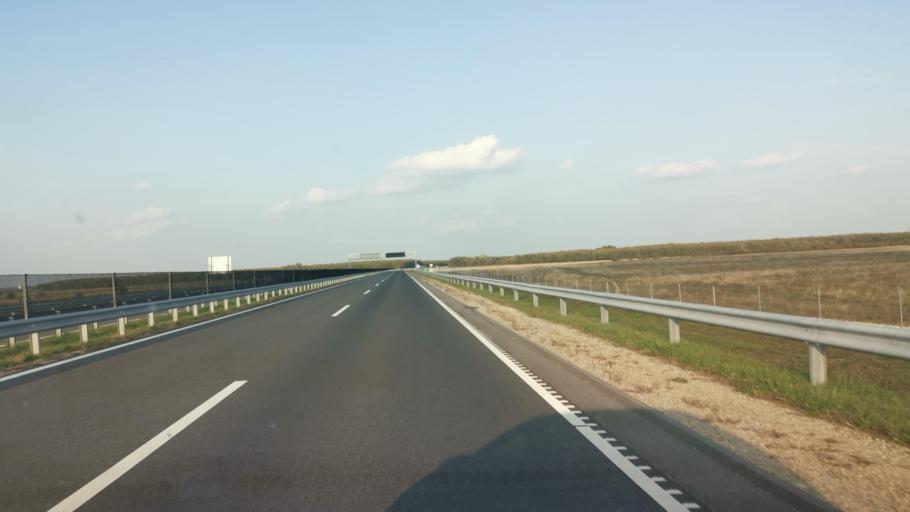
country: HU
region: Gyor-Moson-Sopron
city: Fertoszentmiklos
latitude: 47.5767
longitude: 16.9154
